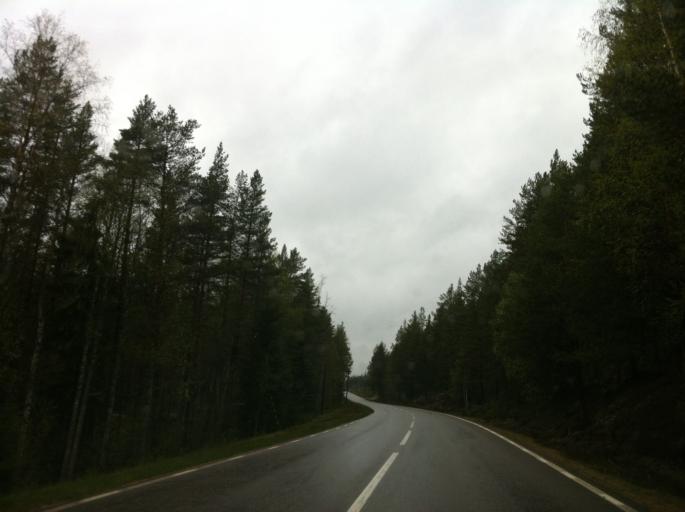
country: SE
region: Jaemtland
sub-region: Harjedalens Kommun
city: Sveg
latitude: 62.1462
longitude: 13.9393
